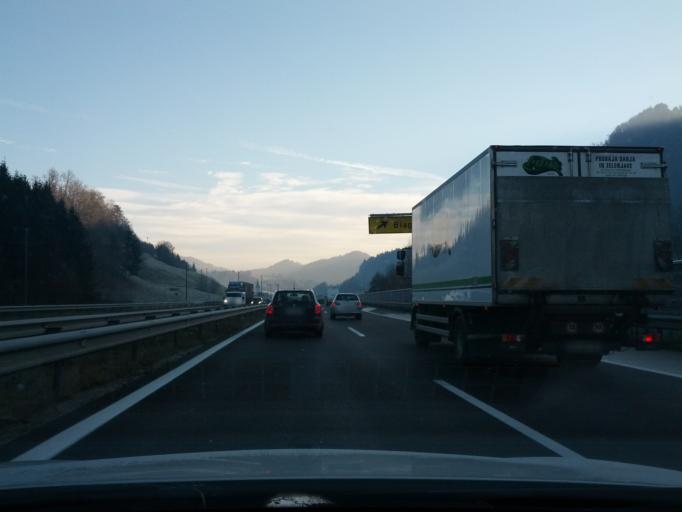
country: SI
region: Moravce
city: Moravce
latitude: 46.1734
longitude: 14.7908
